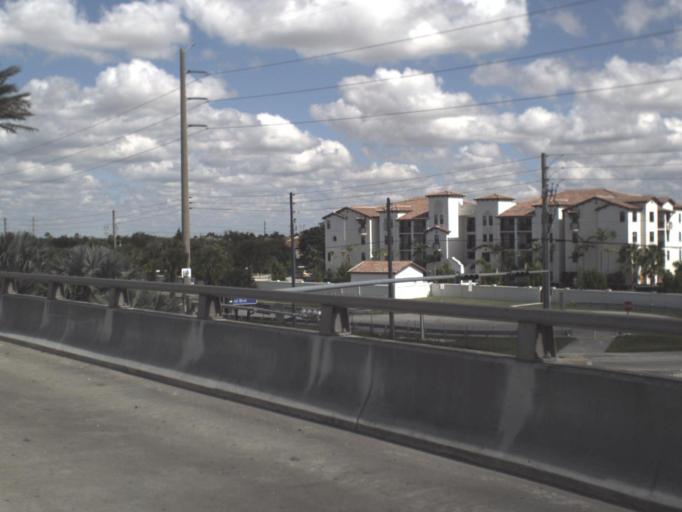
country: US
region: Florida
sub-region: Miami-Dade County
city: Doral
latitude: 25.8116
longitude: -80.3862
